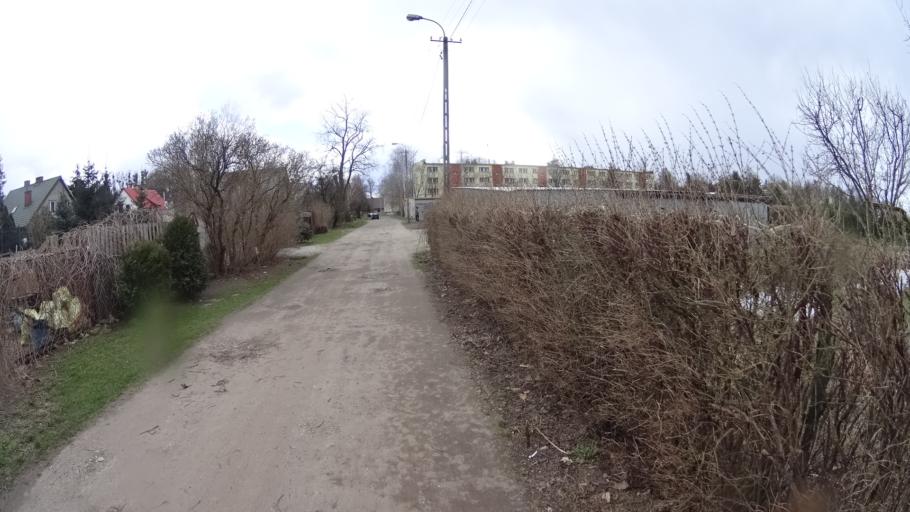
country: PL
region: Masovian Voivodeship
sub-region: Powiat warszawski zachodni
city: Blonie
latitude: 52.2178
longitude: 20.6472
